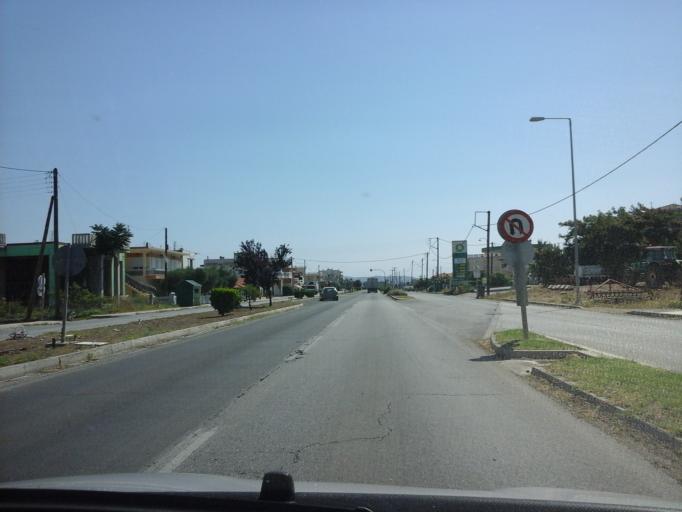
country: GR
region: East Macedonia and Thrace
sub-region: Nomos Evrou
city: Alexandroupoli
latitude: 40.8557
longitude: 25.9318
